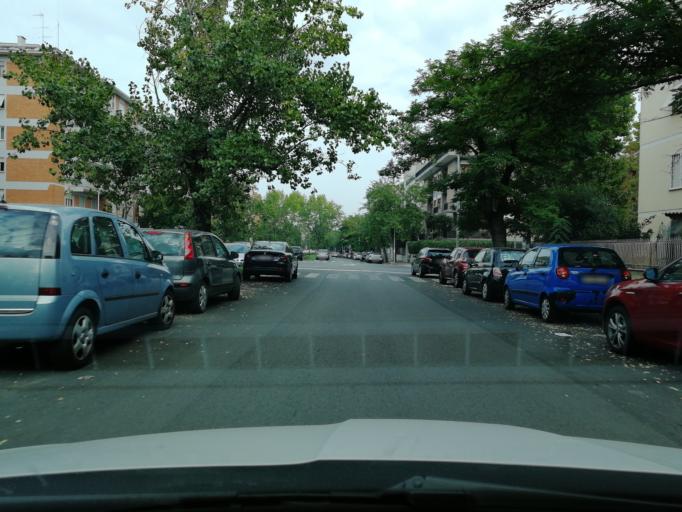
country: IT
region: Latium
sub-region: Citta metropolitana di Roma Capitale
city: Ciampino
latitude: 41.8513
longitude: 12.5650
